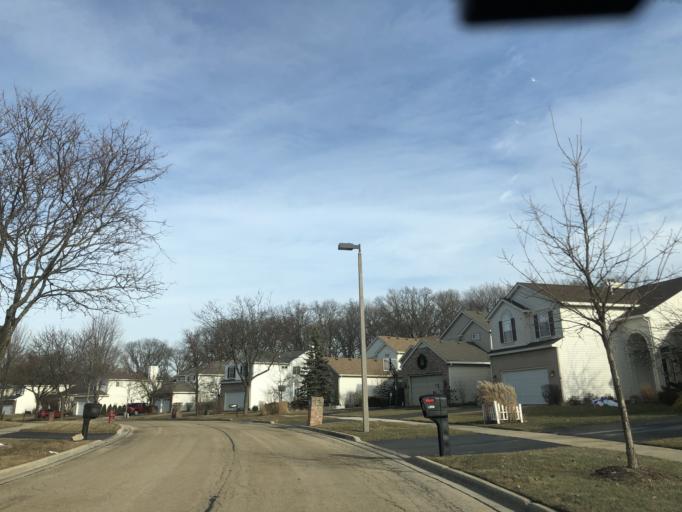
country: US
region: Illinois
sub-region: DuPage County
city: Woodridge
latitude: 41.7192
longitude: -88.0148
